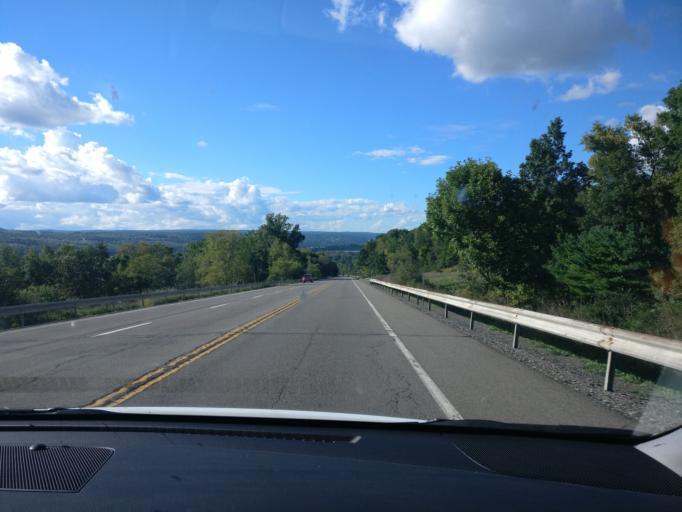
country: US
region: New York
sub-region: Schuyler County
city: Montour Falls
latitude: 42.3421
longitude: -76.8260
